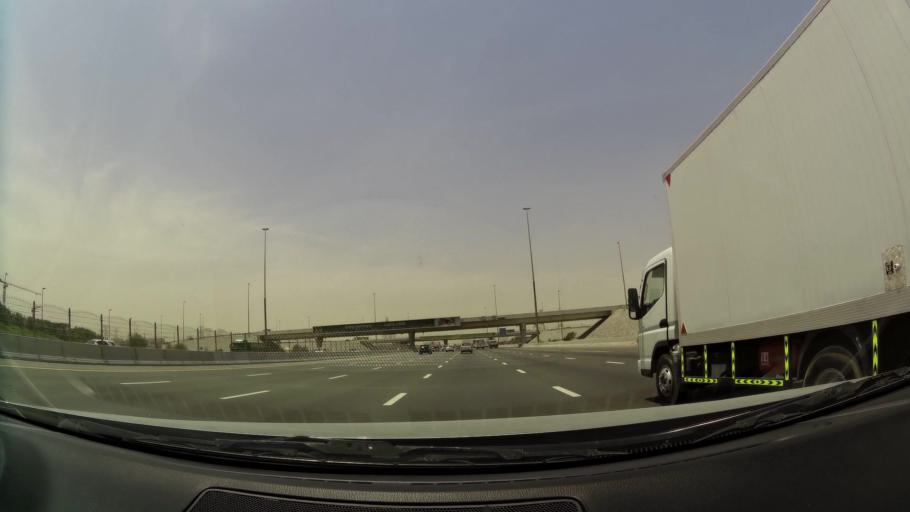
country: AE
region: Ash Shariqah
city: Sharjah
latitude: 25.1630
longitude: 55.3919
